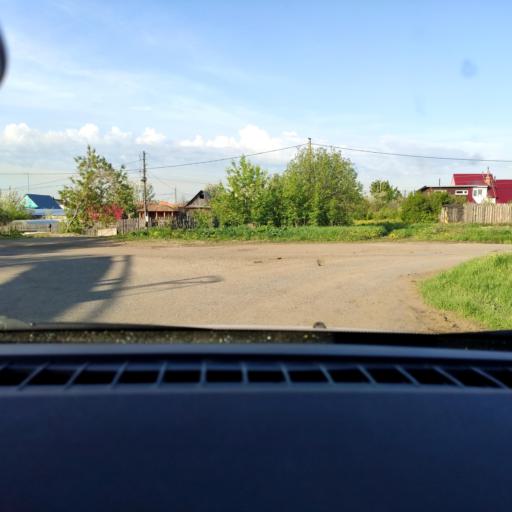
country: RU
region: Perm
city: Kondratovo
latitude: 57.9904
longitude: 56.1103
